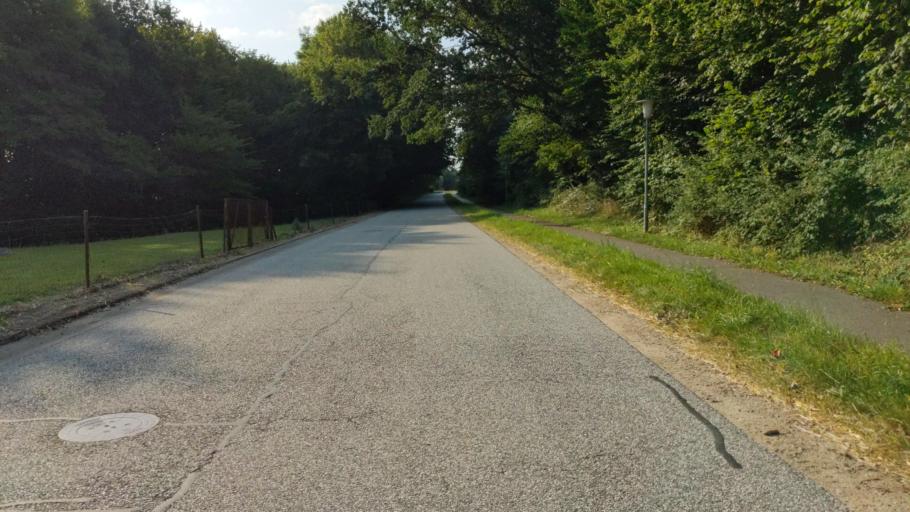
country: DE
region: Mecklenburg-Vorpommern
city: Selmsdorf
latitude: 53.8884
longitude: 10.8867
